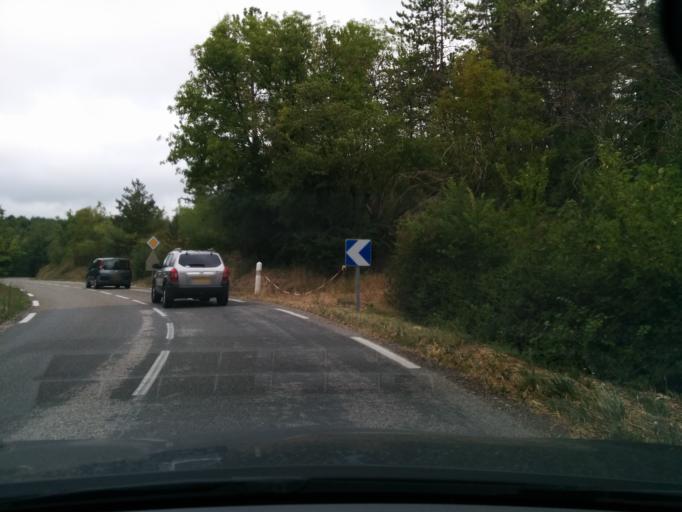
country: FR
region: Midi-Pyrenees
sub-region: Departement du Lot
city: Cahors
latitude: 44.3919
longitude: 1.3636
